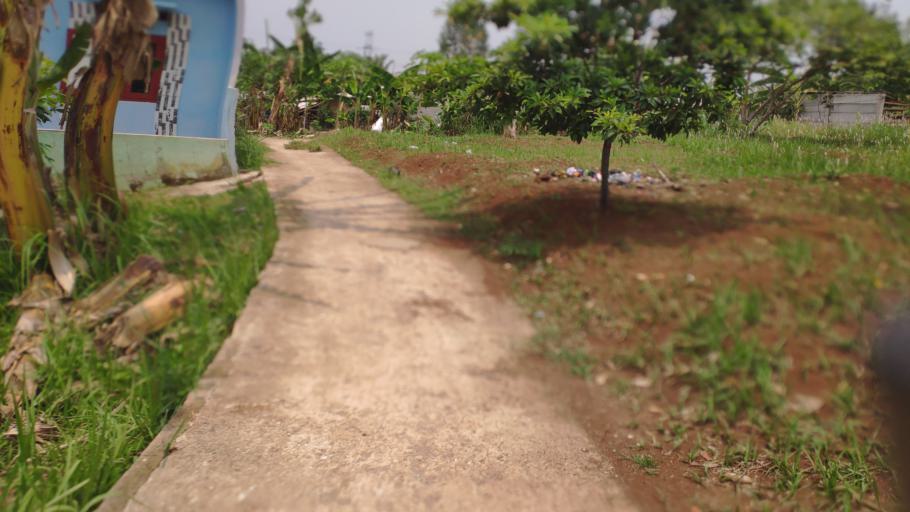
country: ID
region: West Java
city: Sawangan
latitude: -6.3913
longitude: 106.7924
